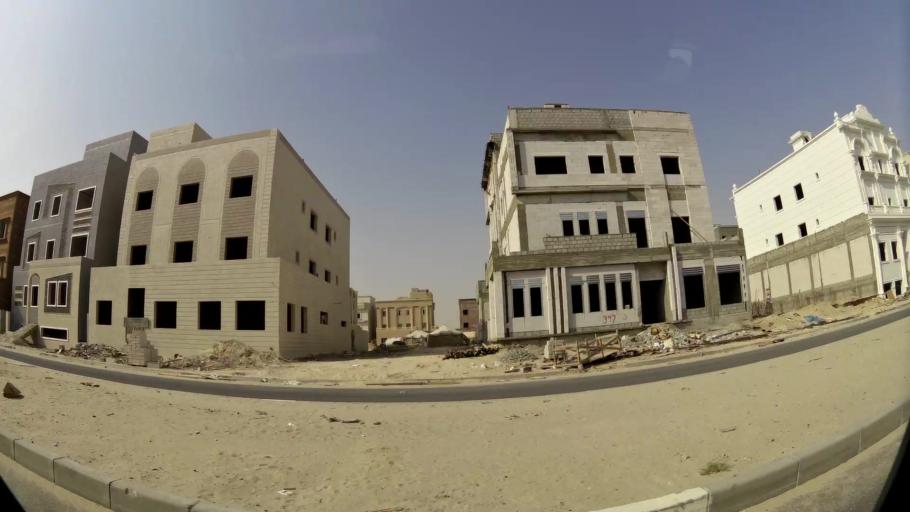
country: KW
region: Muhafazat al Jahra'
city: Al Jahra'
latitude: 29.3553
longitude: 47.7697
